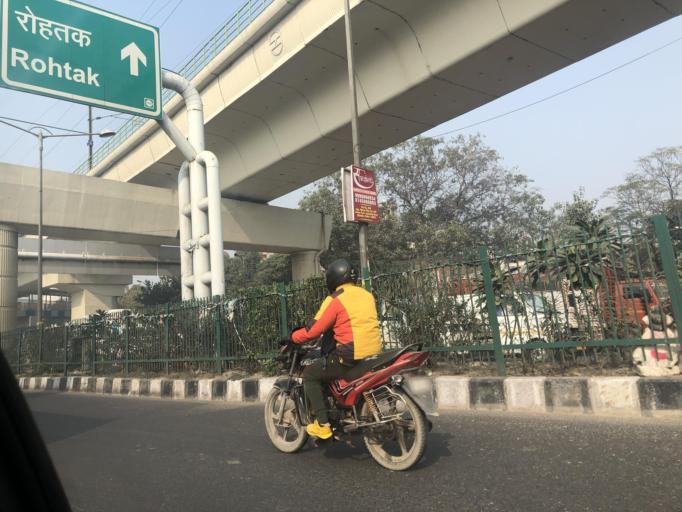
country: IN
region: NCT
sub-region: West Delhi
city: Nangloi Jat
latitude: 28.6820
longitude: 77.0720
